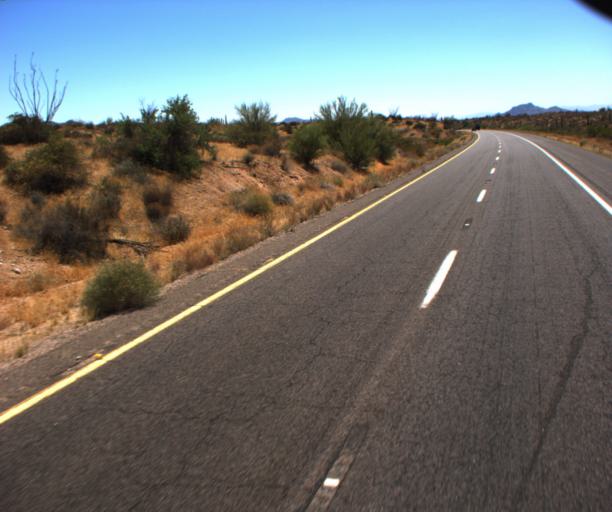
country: US
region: Arizona
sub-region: Maricopa County
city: Rio Verde
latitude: 33.6392
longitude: -111.5456
